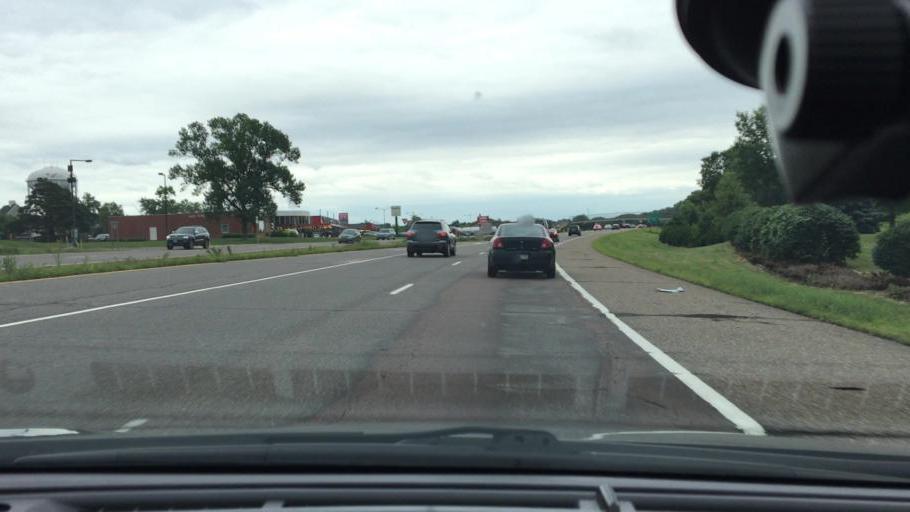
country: US
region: Minnesota
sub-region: Hennepin County
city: Golden Valley
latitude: 44.9847
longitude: -93.3866
